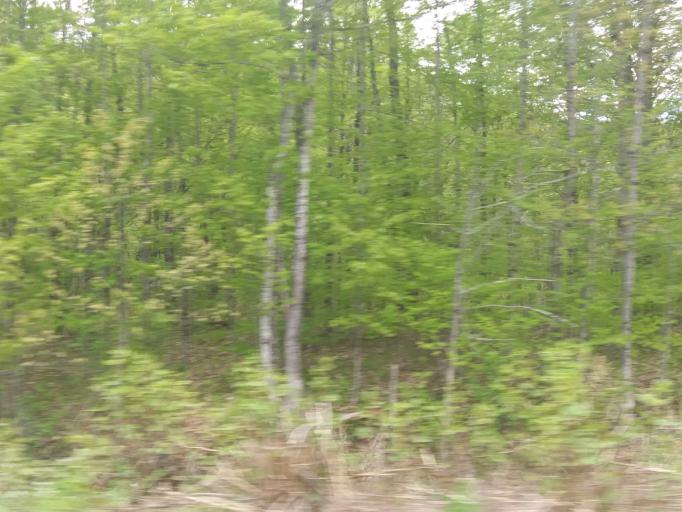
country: US
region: Massachusetts
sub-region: Franklin County
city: Buckland
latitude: 42.5717
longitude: -72.8109
